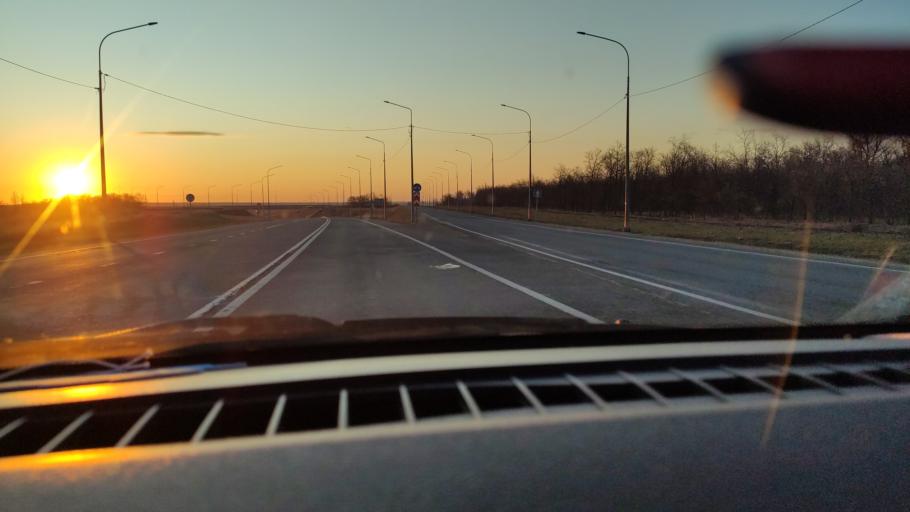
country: RU
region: Saratov
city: Yelshanka
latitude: 51.8196
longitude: 46.3566
